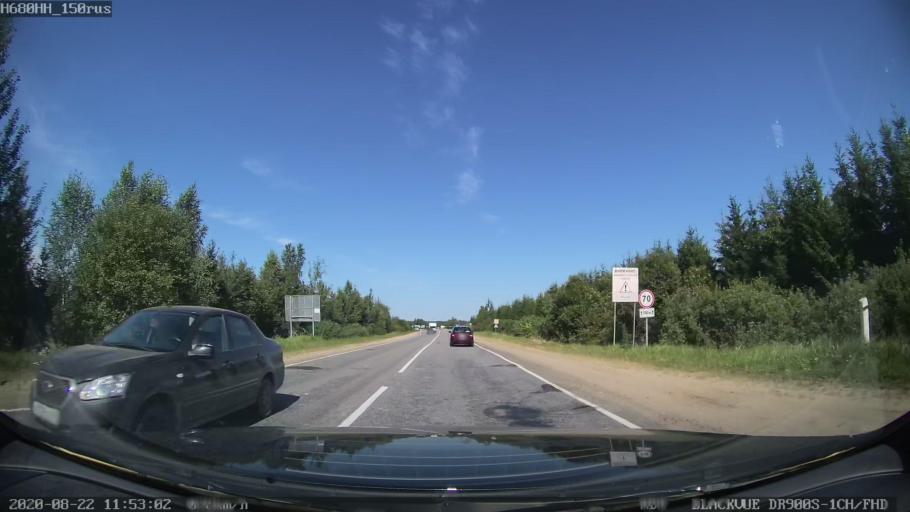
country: RU
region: Tverskaya
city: Vasil'yevskiy Mokh
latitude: 57.1223
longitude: 36.1135
